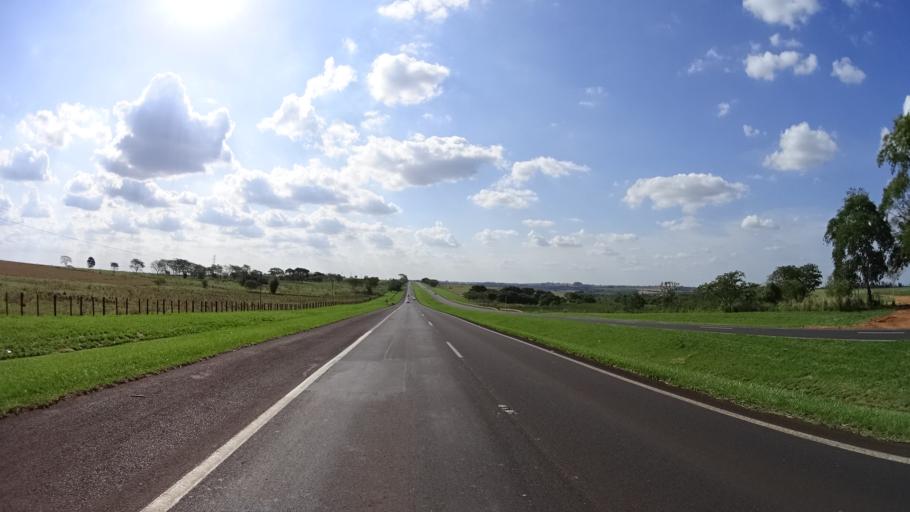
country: BR
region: Sao Paulo
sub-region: Guapiacu
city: Guapiacu
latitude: -20.9790
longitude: -49.2213
